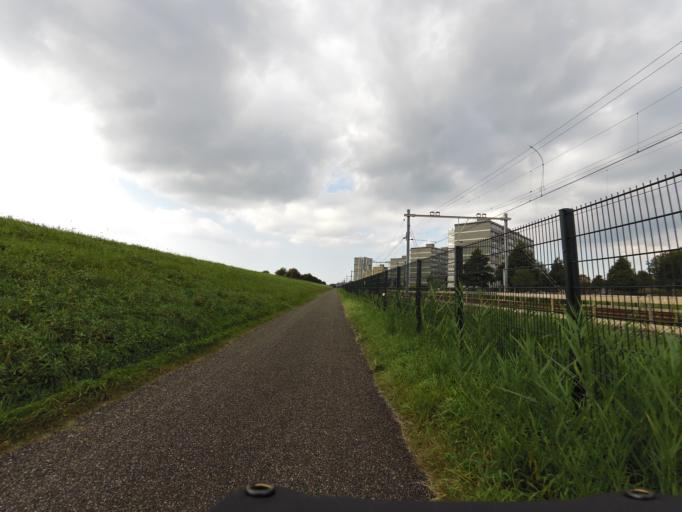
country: NL
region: South Holland
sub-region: Gemeente Maassluis
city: Maassluis
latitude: 51.9273
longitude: 4.2332
